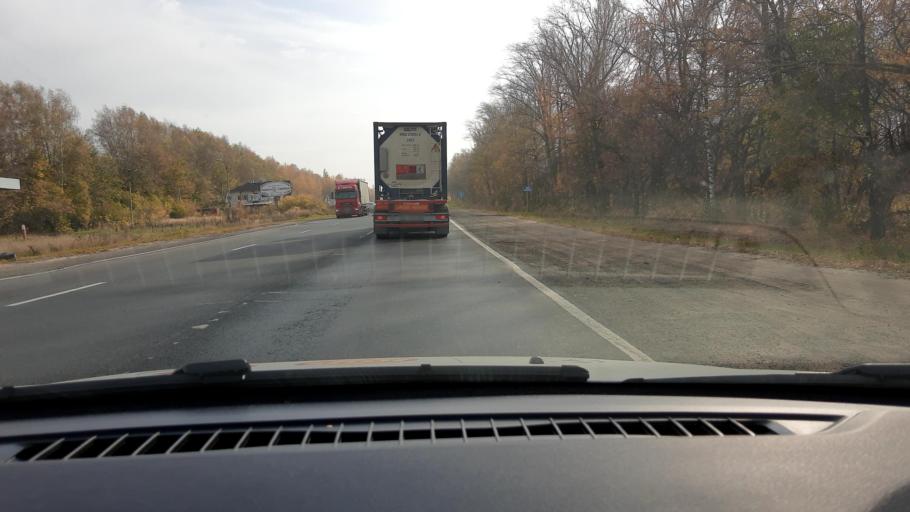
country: RU
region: Nizjnij Novgorod
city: Kstovo
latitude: 56.1181
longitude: 44.2753
